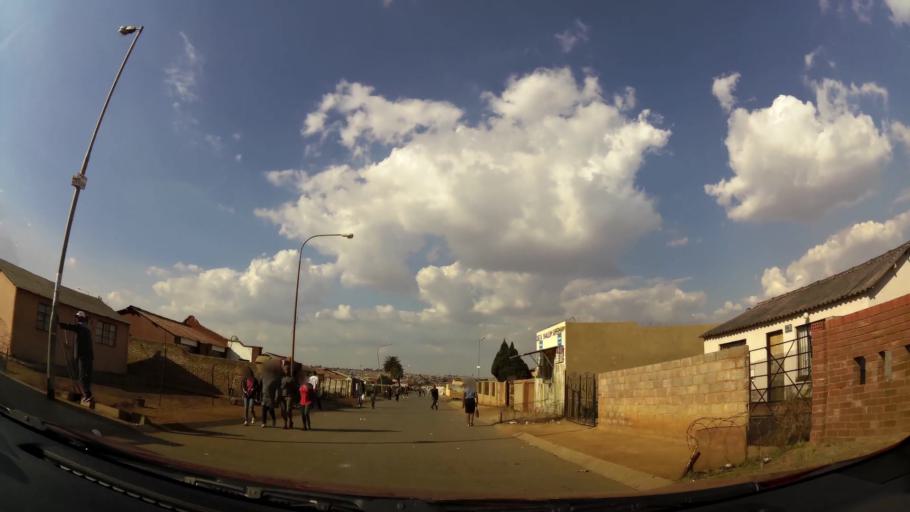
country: ZA
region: Gauteng
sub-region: City of Johannesburg Metropolitan Municipality
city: Soweto
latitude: -26.2237
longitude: 27.8669
